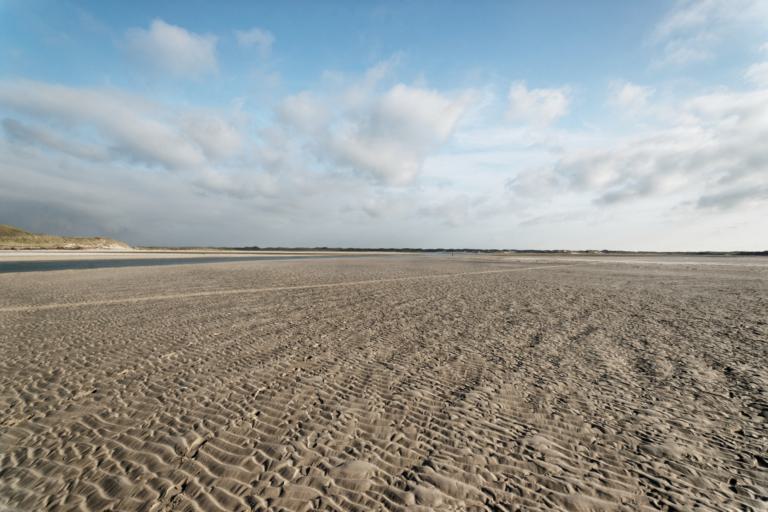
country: NL
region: North Holland
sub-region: Gemeente Texel
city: Den Burg
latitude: 53.1385
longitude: 4.7980
